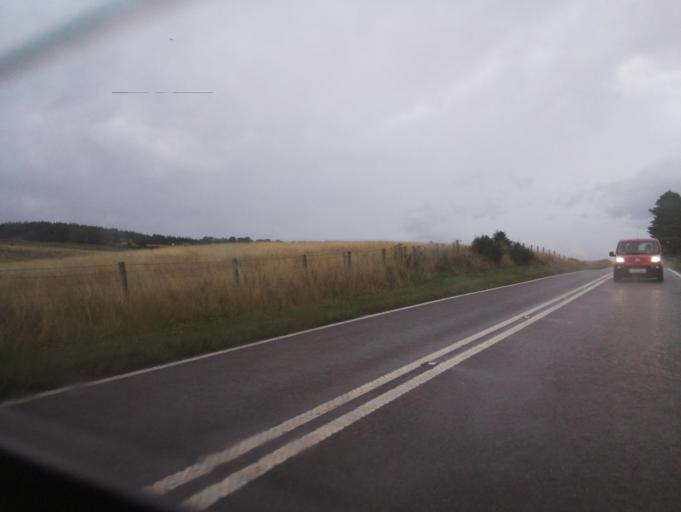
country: GB
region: Scotland
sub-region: Highland
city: Grantown on Spey
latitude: 57.2679
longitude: -3.7254
